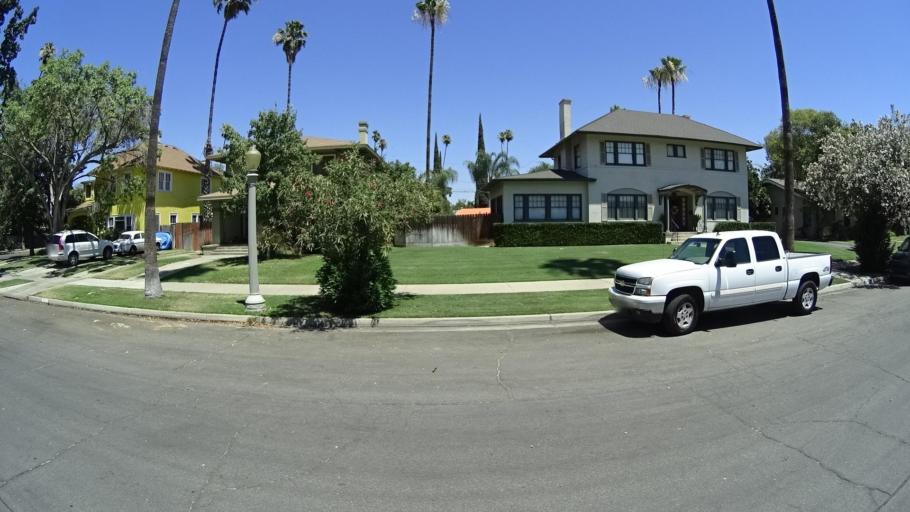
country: US
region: California
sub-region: Fresno County
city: Fresno
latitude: 36.7406
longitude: -119.7655
